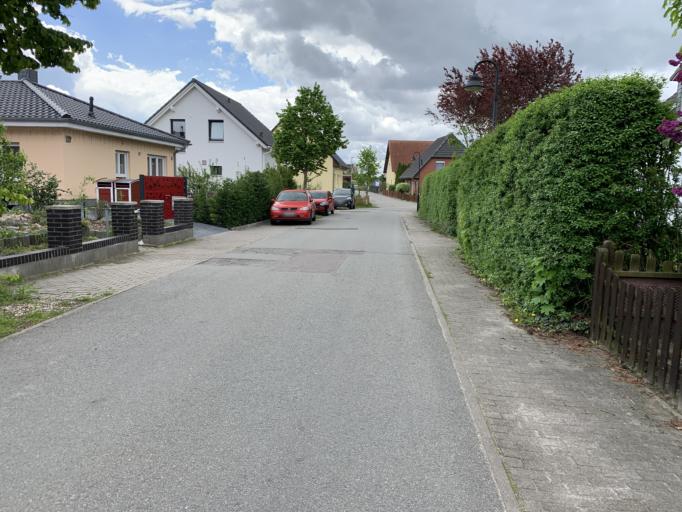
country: DE
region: Brandenburg
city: Gross Kreutz
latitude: 52.3901
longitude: 12.7034
